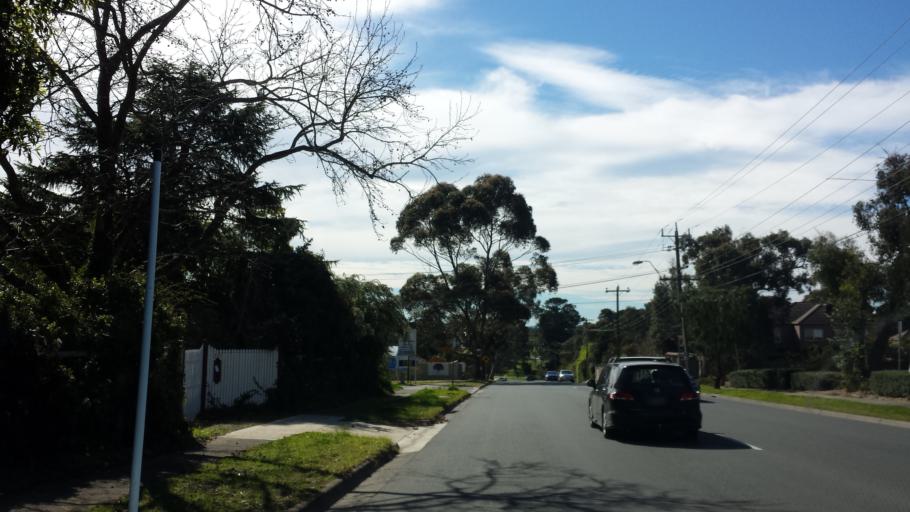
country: AU
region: Victoria
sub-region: Maroondah
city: Warranwood
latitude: -37.7906
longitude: 145.2359
